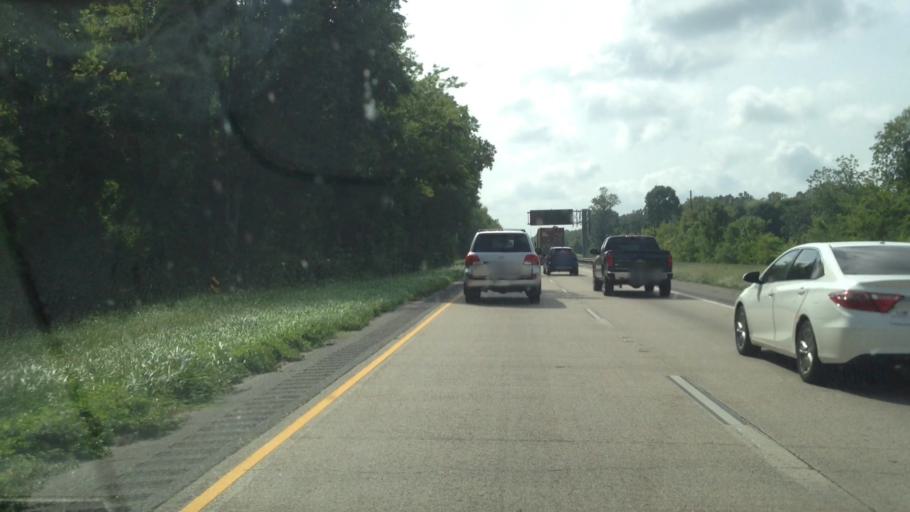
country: US
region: Louisiana
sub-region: Ascension Parish
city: Sorrento
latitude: 30.1849
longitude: -90.9053
